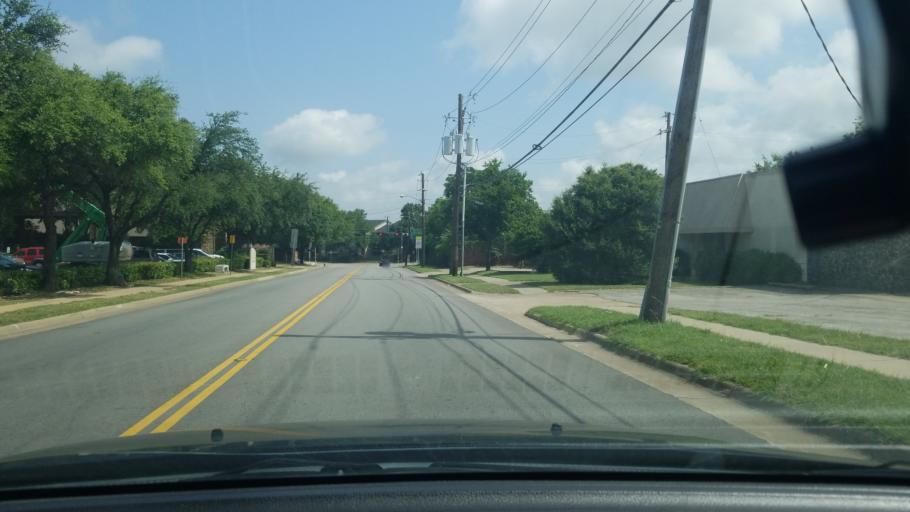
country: US
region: Texas
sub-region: Dallas County
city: Mesquite
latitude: 32.8056
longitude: -96.6889
